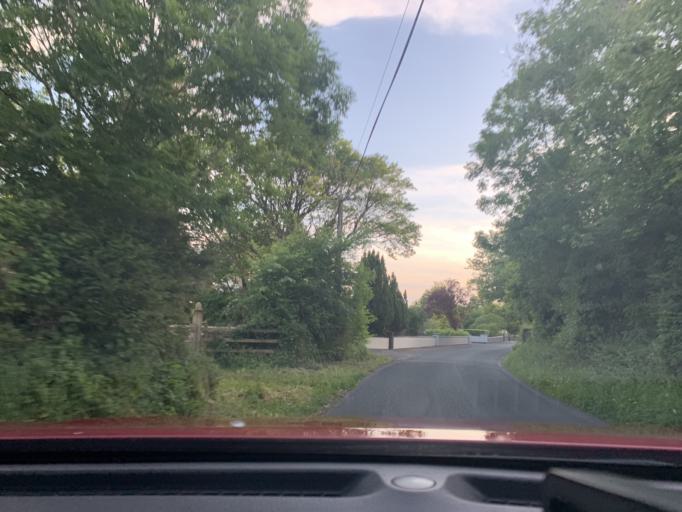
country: IE
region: Connaught
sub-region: Sligo
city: Sligo
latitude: 54.2898
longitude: -8.4495
